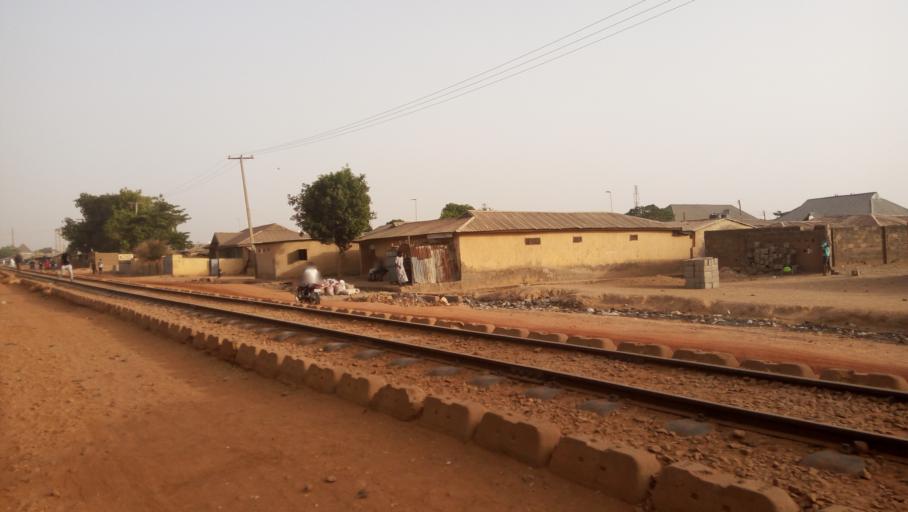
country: NG
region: Kaduna
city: Zaria
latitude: 11.1626
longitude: 7.6542
